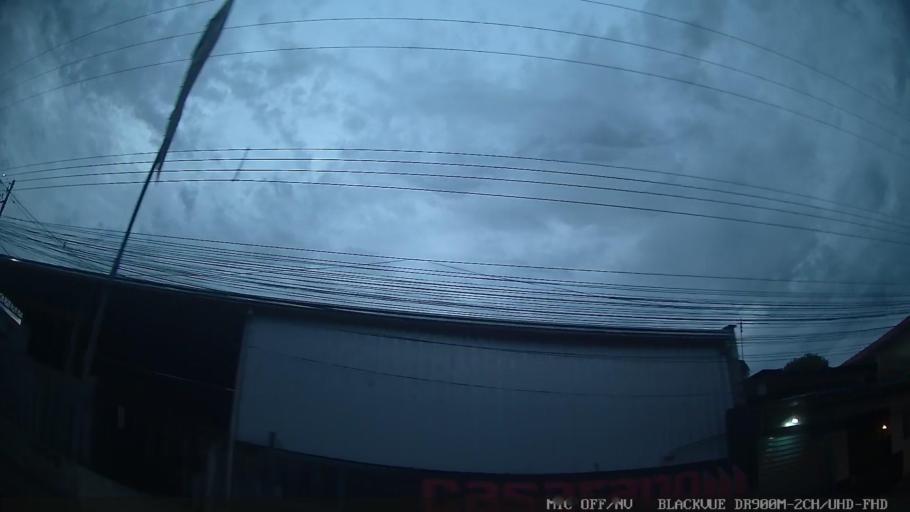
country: BR
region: Sao Paulo
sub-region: Itatiba
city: Itatiba
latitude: -22.8742
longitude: -46.7929
